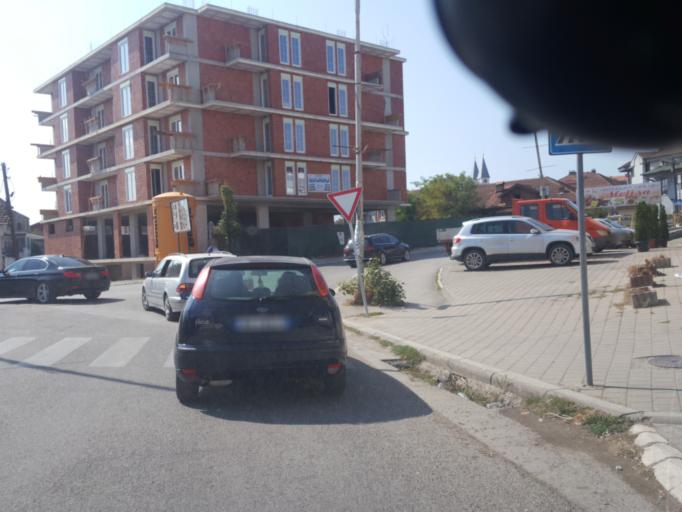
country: XK
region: Gjakova
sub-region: Komuna e Gjakoves
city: Gjakove
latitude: 42.3760
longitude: 20.4290
